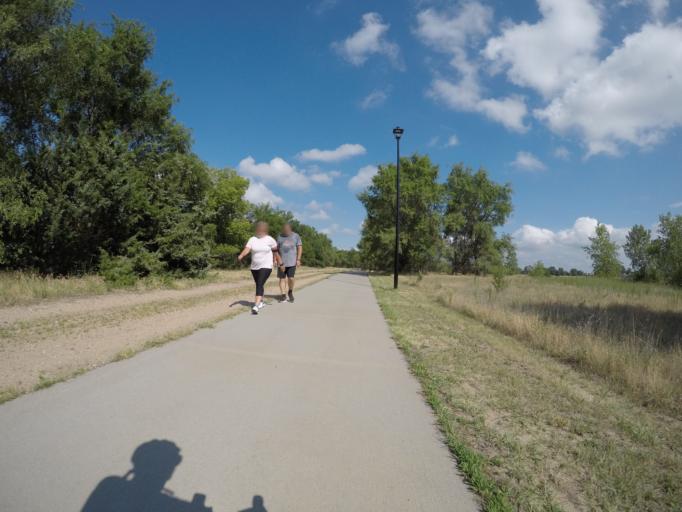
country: US
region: Nebraska
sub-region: Buffalo County
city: Kearney
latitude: 40.6730
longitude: -99.0447
